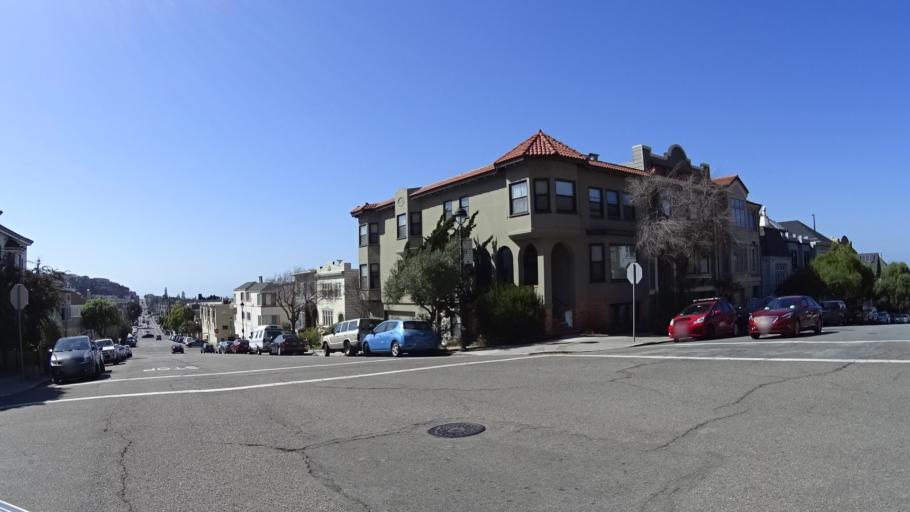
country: US
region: California
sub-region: San Francisco County
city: San Francisco
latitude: 37.7605
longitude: -122.4617
